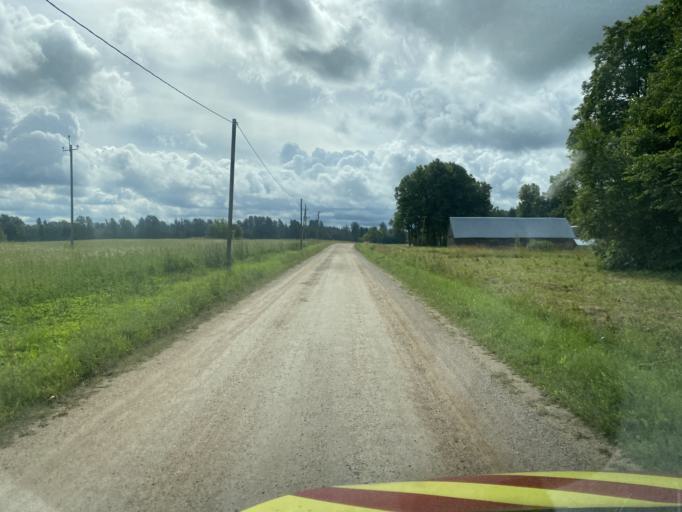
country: EE
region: Viljandimaa
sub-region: Karksi vald
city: Karksi-Nuia
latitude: 58.0646
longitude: 25.5294
